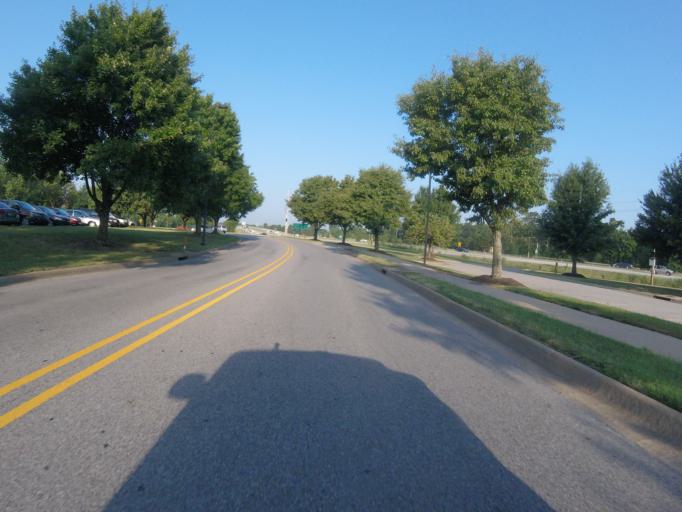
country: US
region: Arkansas
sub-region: Washington County
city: Johnson
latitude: 36.1129
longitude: -94.1566
